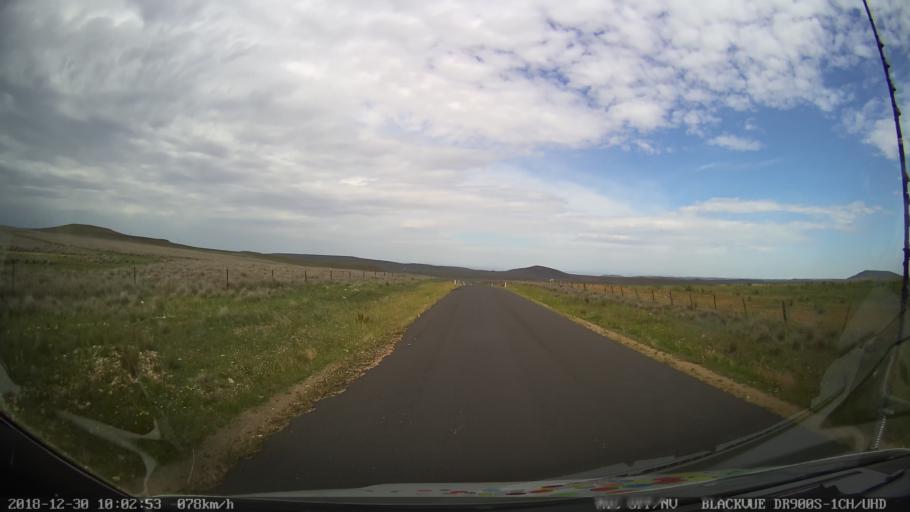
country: AU
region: New South Wales
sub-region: Cooma-Monaro
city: Cooma
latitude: -36.5154
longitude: 149.1655
